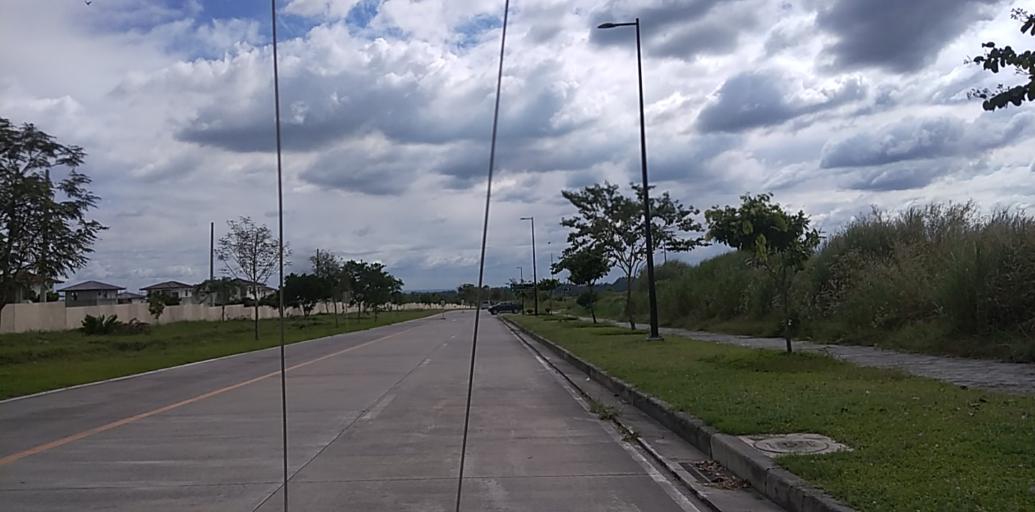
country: PH
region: Central Luzon
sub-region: Province of Pampanga
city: Dolores
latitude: 15.1147
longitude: 120.5126
